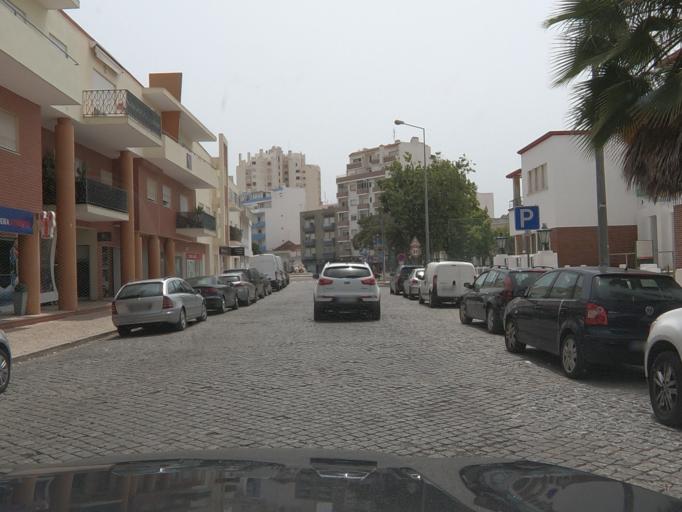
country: PT
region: Faro
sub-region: Portimao
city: Portimao
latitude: 37.1323
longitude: -8.5361
